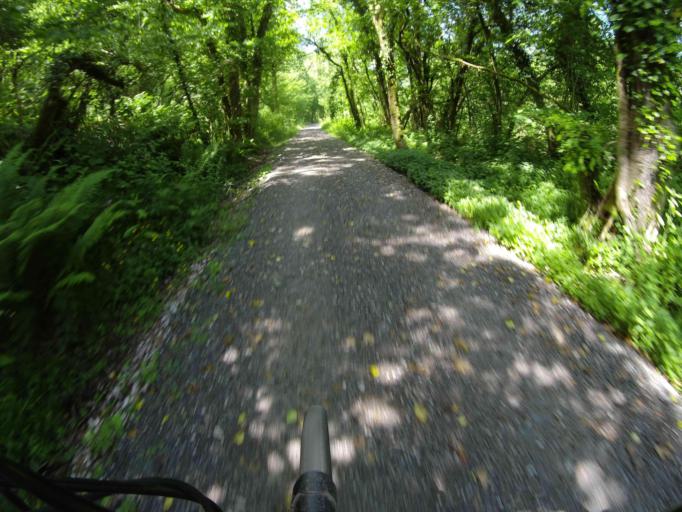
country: GB
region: England
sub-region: Devon
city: Bovey Tracey
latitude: 50.6324
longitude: -3.7297
